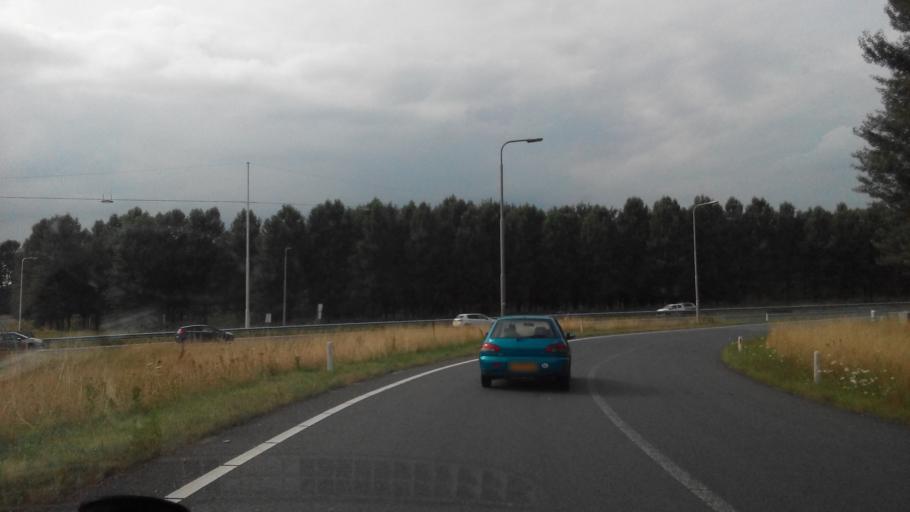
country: NL
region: Flevoland
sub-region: Gemeente Almere
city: Almere Stad
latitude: 52.3721
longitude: 5.2882
